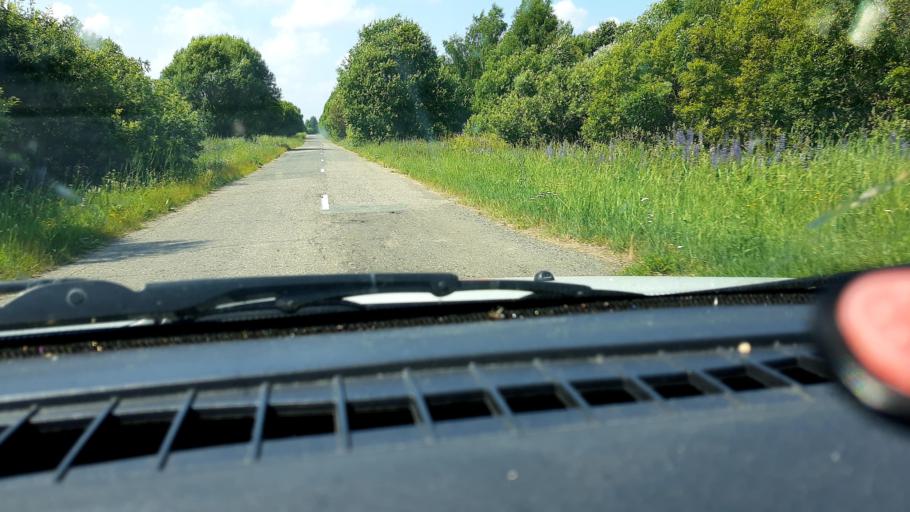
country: RU
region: Nizjnij Novgorod
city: Sharanga
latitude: 57.0594
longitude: 46.6071
